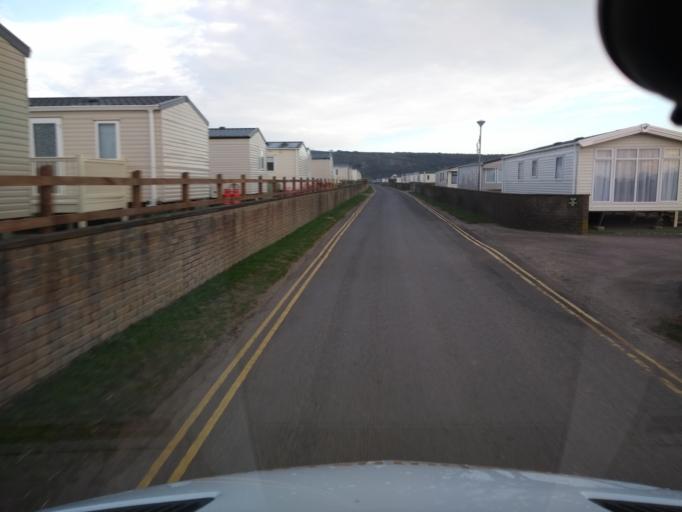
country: GB
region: England
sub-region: North Somerset
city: Weston-super-Mare
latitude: 51.3163
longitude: -3.0101
